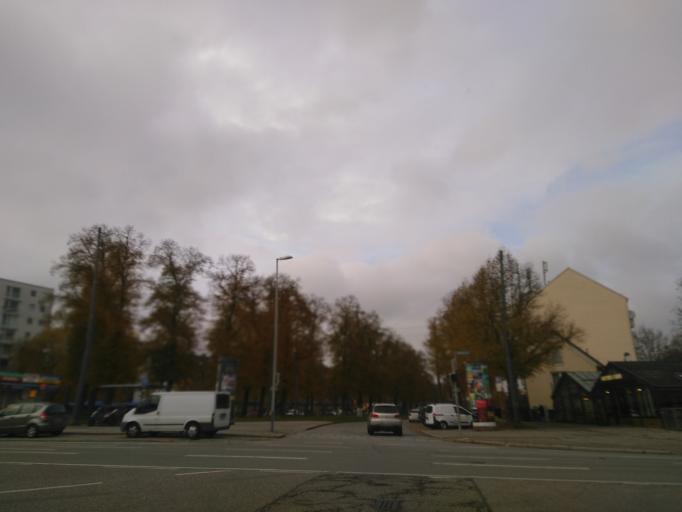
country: DE
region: Bavaria
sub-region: Upper Bavaria
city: Unterhaching
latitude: 48.1026
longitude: 11.5976
